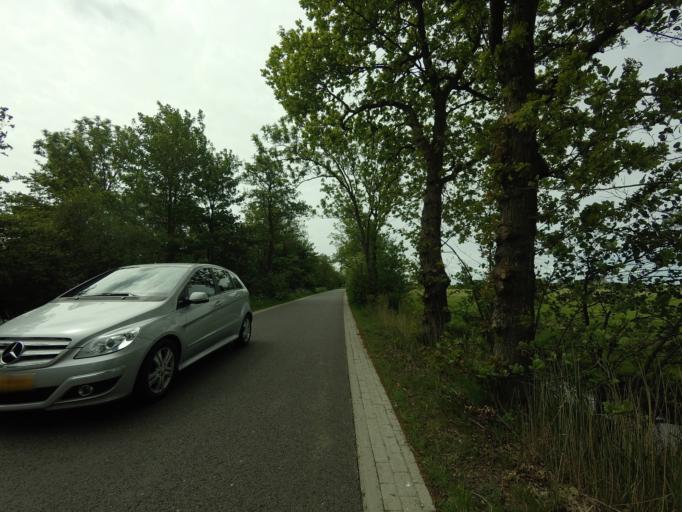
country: NL
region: Friesland
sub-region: Sudwest Fryslan
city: Koudum
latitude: 52.9031
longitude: 5.4640
